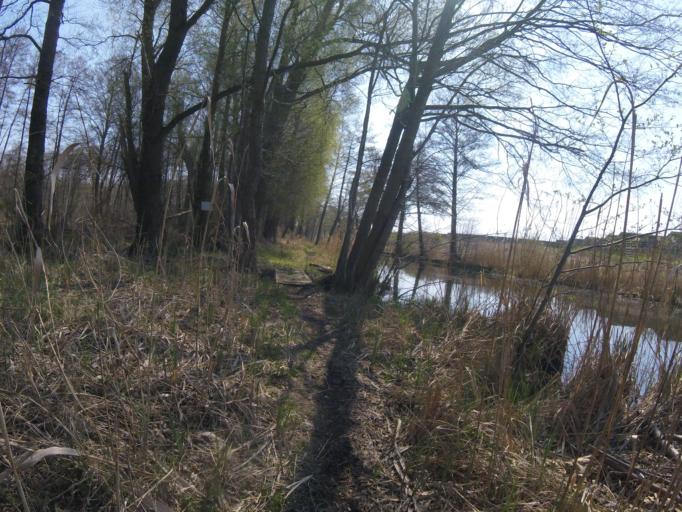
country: DE
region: Brandenburg
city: Mittenwalde
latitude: 52.2544
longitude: 13.5383
